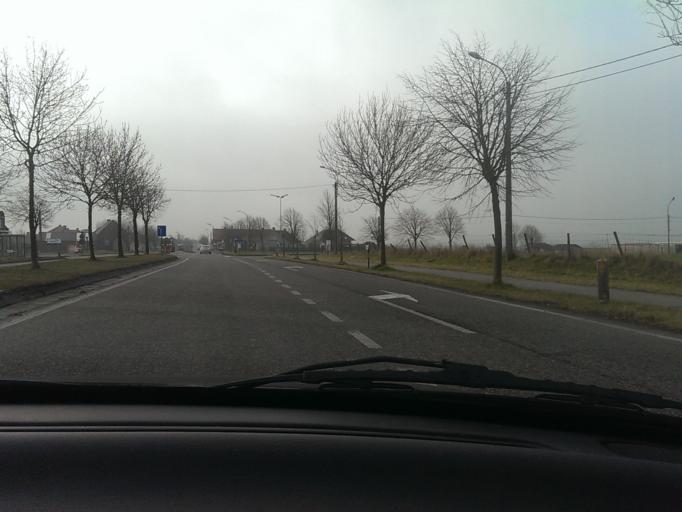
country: BE
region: Flanders
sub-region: Provincie West-Vlaanderen
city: Ledegem
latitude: 50.8766
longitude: 3.1119
